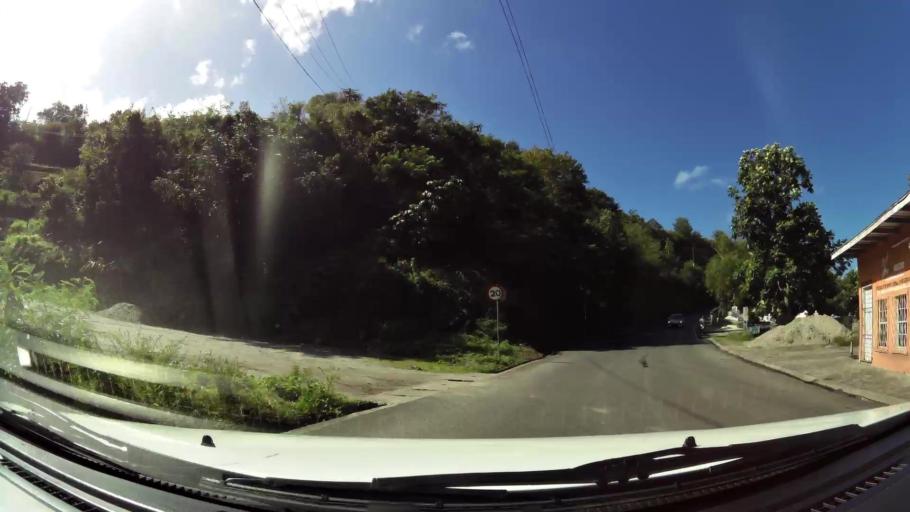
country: LC
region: Choiseul Quarter
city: Choiseul
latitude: 13.7728
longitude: -61.0483
